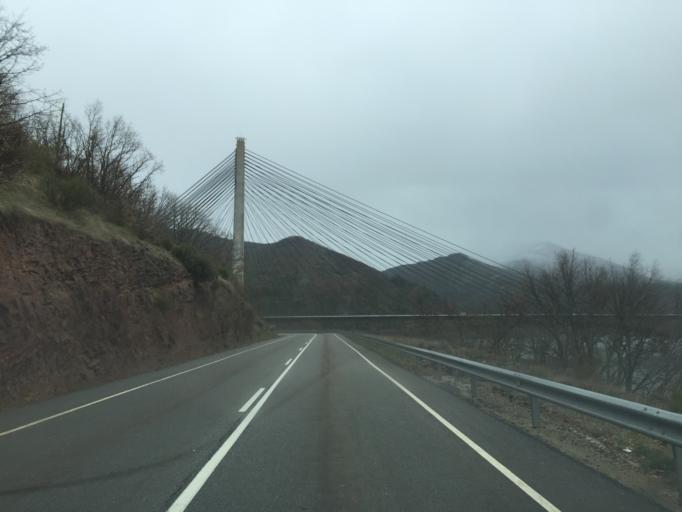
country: ES
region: Castille and Leon
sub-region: Provincia de Leon
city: Sena de Luna
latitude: 42.8972
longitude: -5.8927
